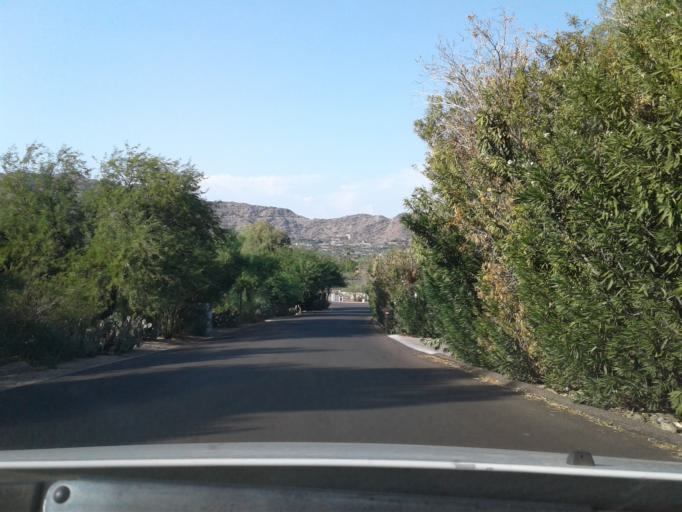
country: US
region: Arizona
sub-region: Maricopa County
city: Paradise Valley
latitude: 33.5226
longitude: -111.9585
